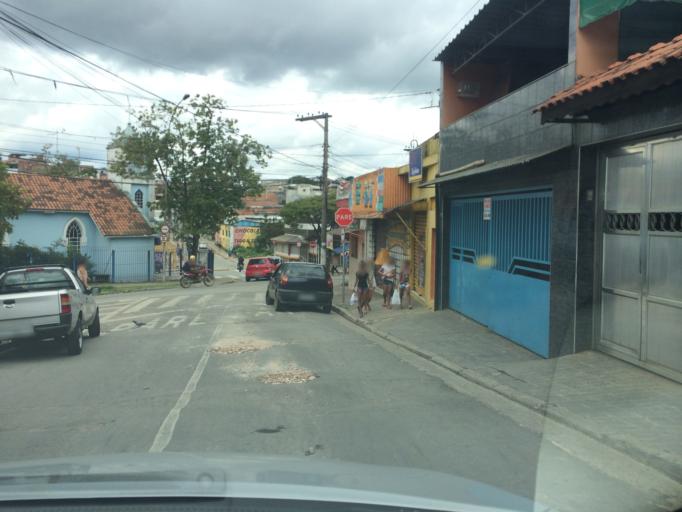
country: BR
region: Sao Paulo
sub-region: Guarulhos
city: Guarulhos
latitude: -23.4295
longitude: -46.5220
